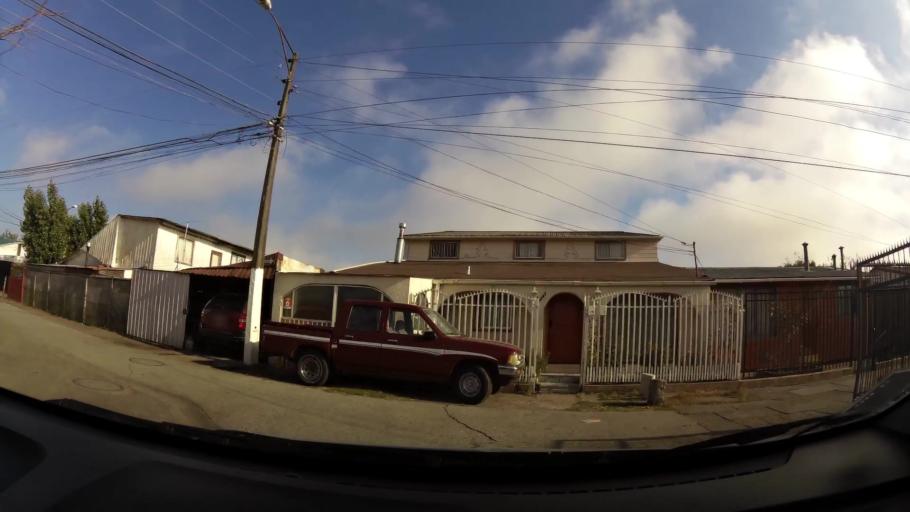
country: CL
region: Biobio
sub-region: Provincia de Concepcion
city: Concepcion
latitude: -36.7879
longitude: -73.1009
